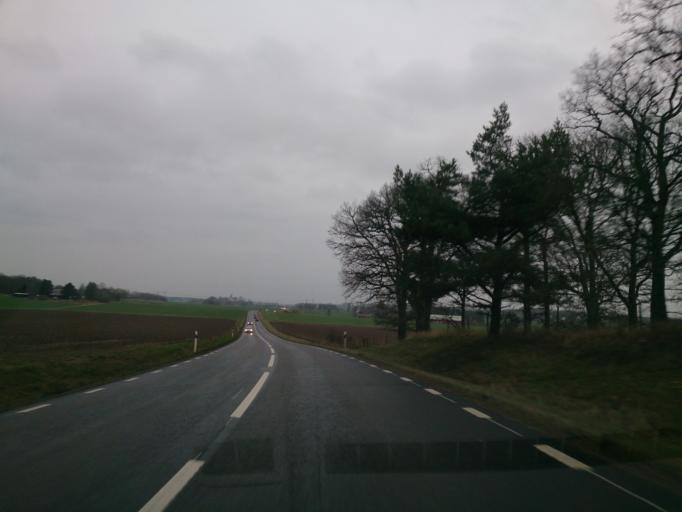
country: SE
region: OEstergoetland
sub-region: Linkopings Kommun
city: Linghem
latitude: 58.3867
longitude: 15.7838
